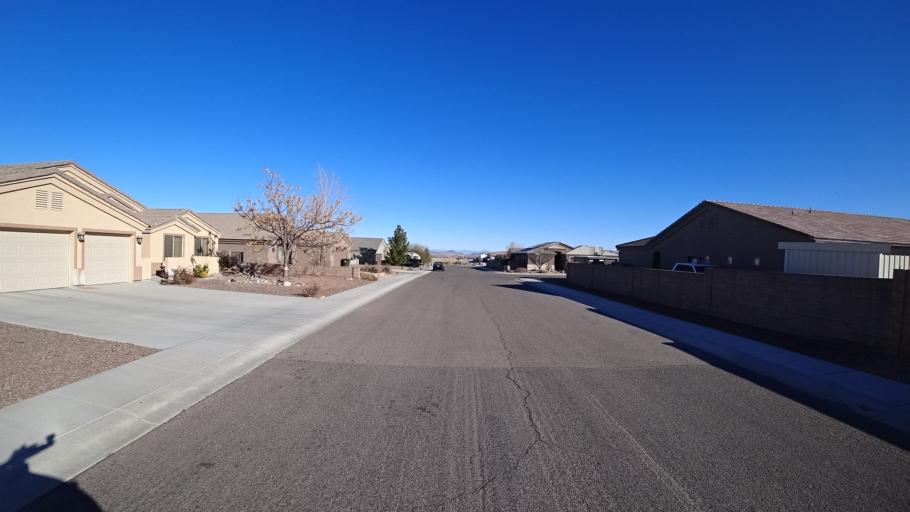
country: US
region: Arizona
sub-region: Mohave County
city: Kingman
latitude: 35.1867
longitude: -114.0021
